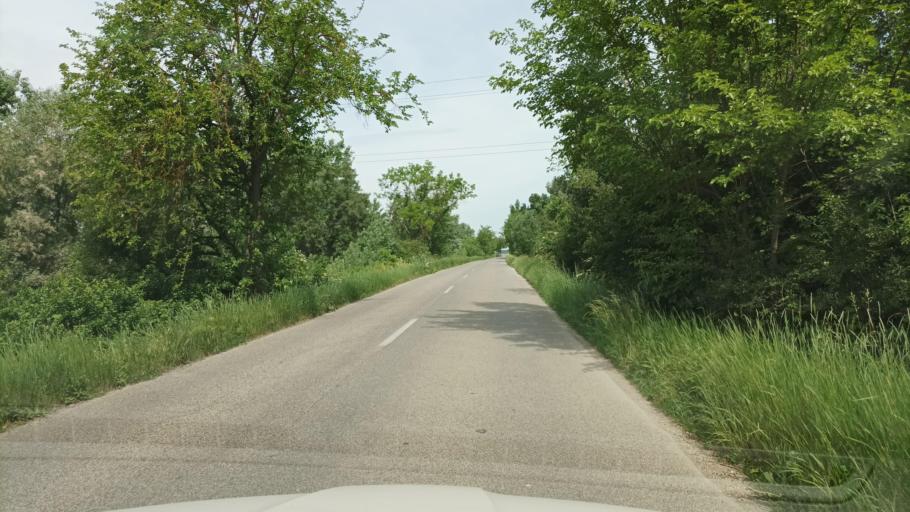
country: HU
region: Pest
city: Rackeve
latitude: 47.0970
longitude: 18.9274
